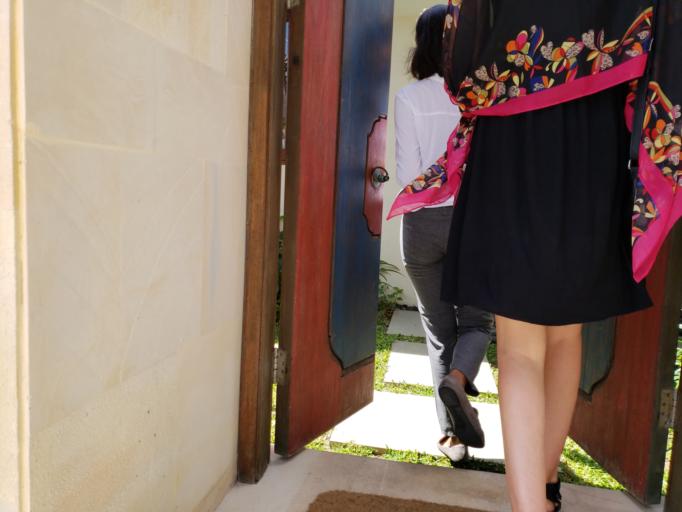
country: ID
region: Bali
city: Kangin
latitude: -8.8447
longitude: 115.1312
